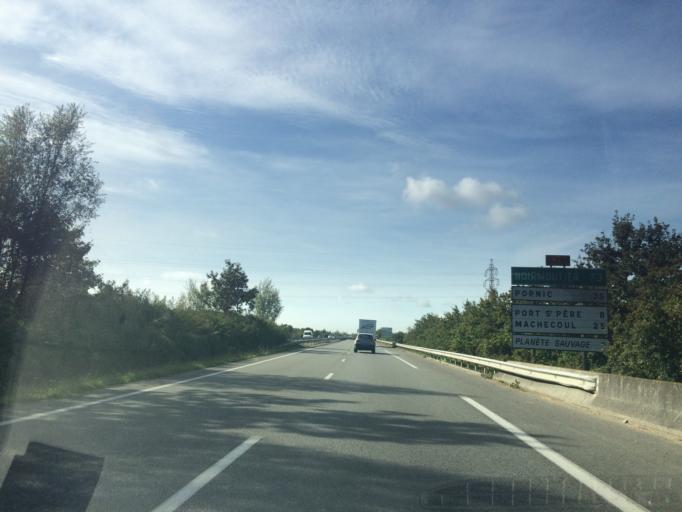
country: FR
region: Pays de la Loire
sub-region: Departement de la Loire-Atlantique
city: La Montagne
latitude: 47.1720
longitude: -1.6753
